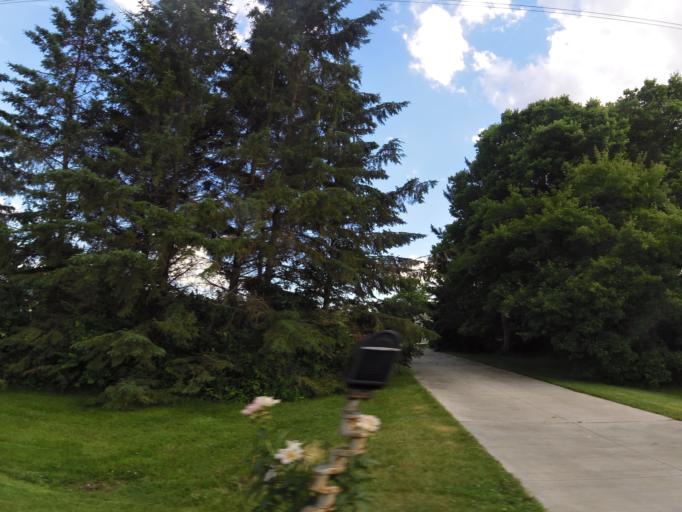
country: US
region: Minnesota
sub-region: Scott County
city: Prior Lake
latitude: 44.6887
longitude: -93.4712
